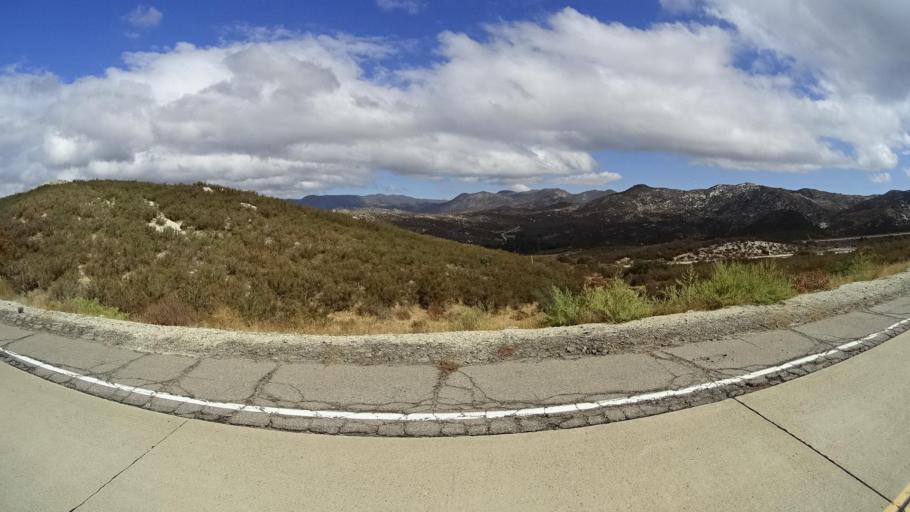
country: US
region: California
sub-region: San Diego County
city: Campo
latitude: 32.7194
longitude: -116.3980
